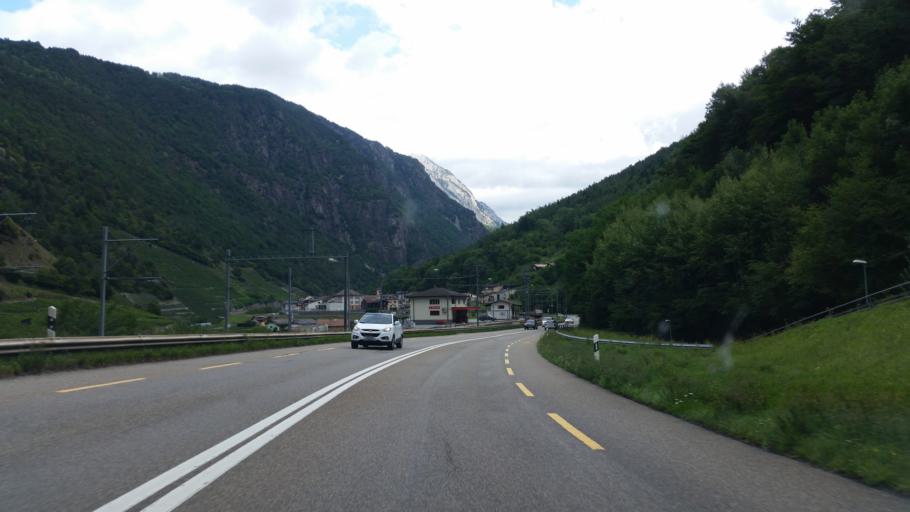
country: CH
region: Valais
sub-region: Martigny District
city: Martigny-Ville
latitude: 46.0783
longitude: 7.0799
